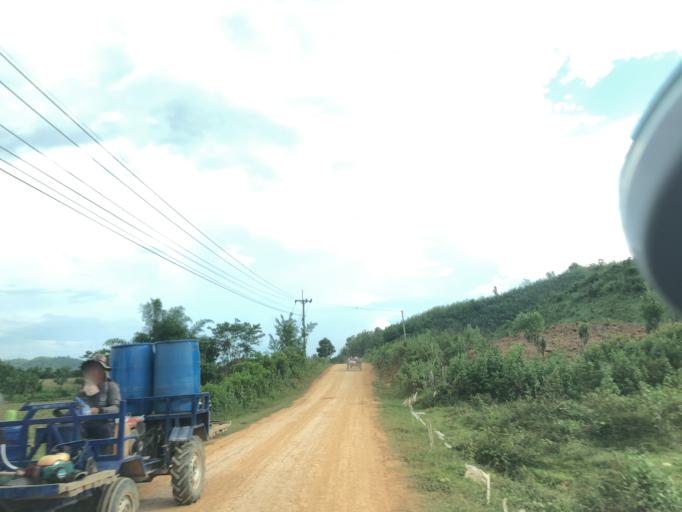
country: TH
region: Loei
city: Chiang Khan
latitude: 17.9988
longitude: 101.4194
